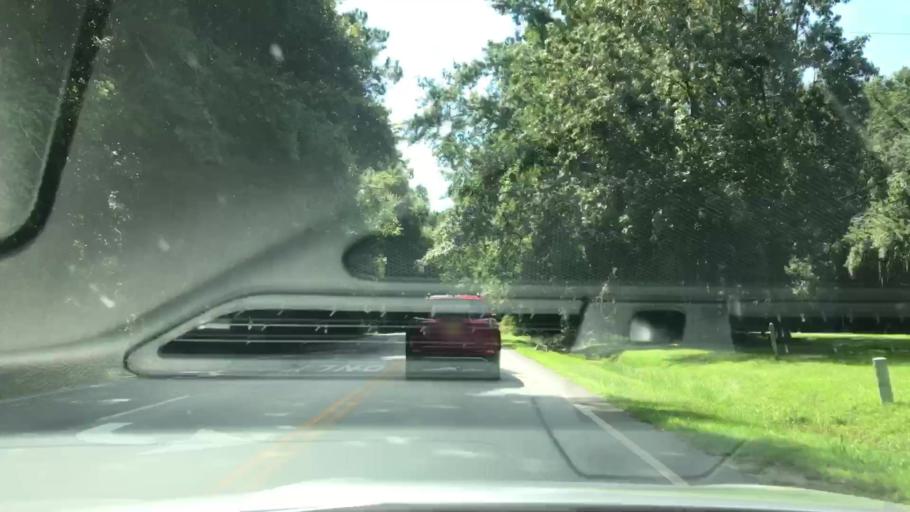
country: US
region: South Carolina
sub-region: Charleston County
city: Shell Point
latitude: 32.8544
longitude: -80.0710
